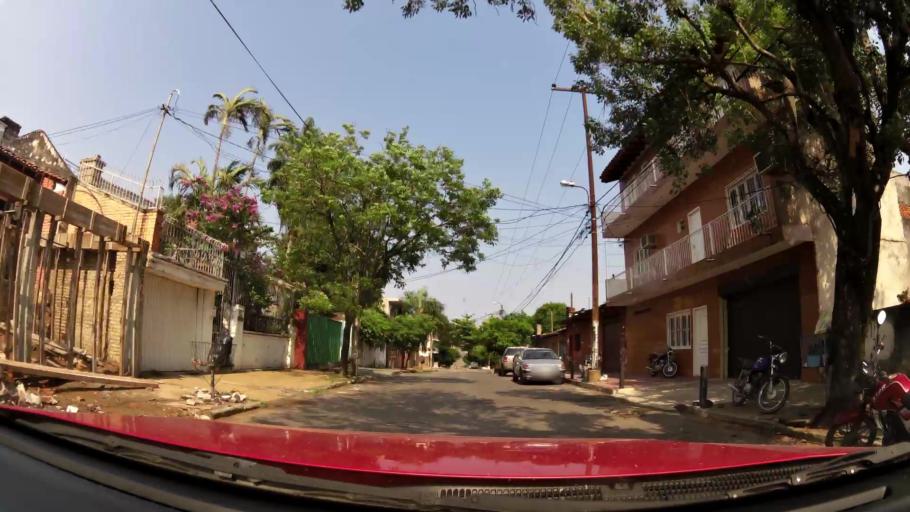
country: PY
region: Presidente Hayes
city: Nanawa
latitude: -25.2814
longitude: -57.6571
